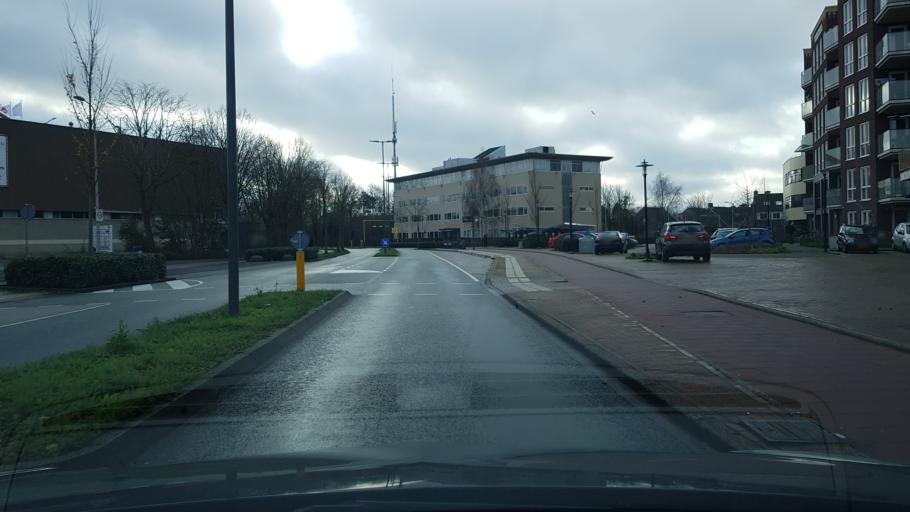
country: NL
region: South Holland
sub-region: Gemeente Lisse
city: Lisse
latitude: 52.2575
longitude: 4.5583
